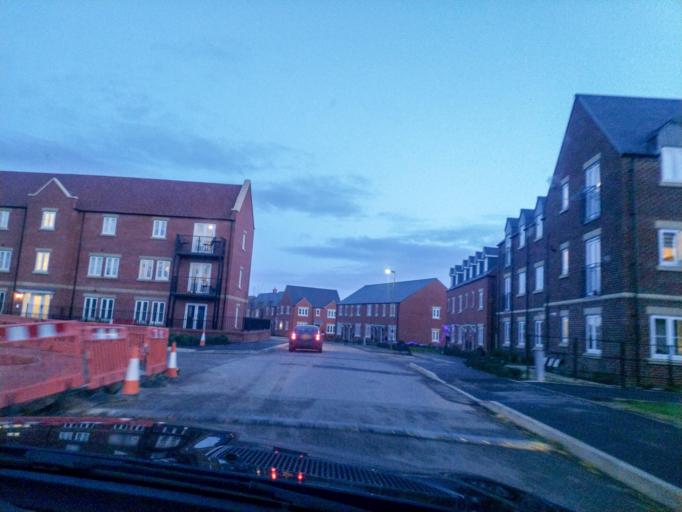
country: GB
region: England
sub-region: Oxfordshire
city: Adderbury
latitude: 52.0423
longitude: -1.3235
